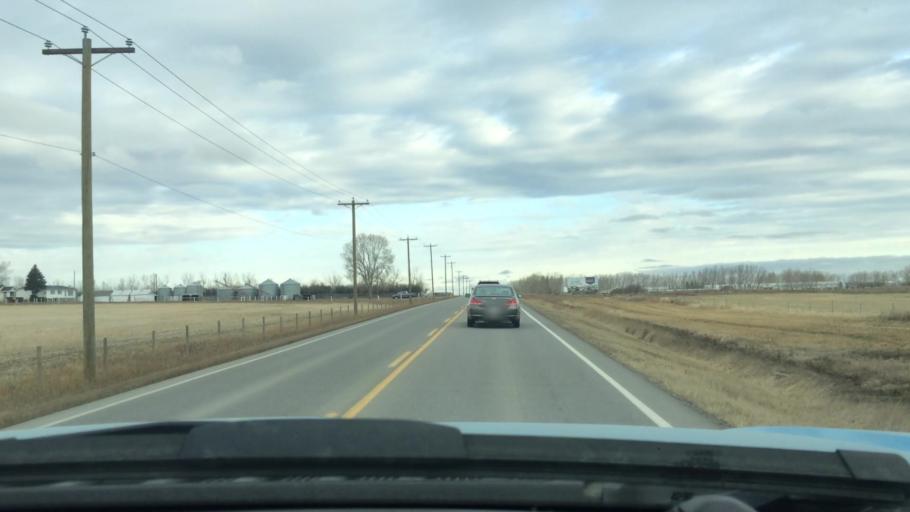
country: CA
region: Alberta
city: Airdrie
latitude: 51.2255
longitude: -114.0249
